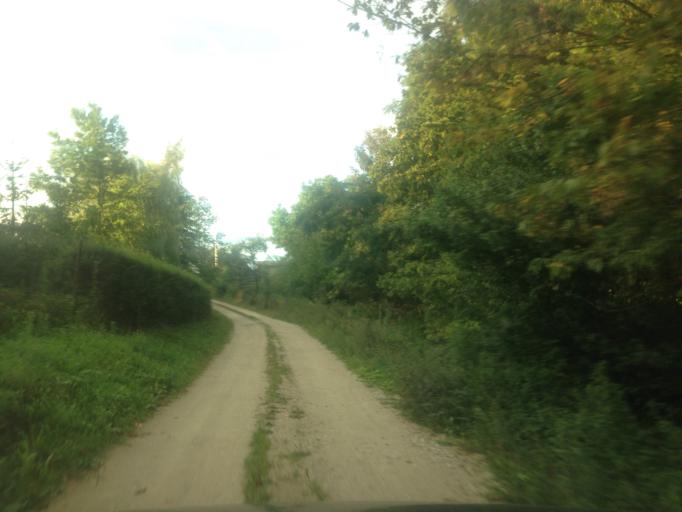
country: PL
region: Kujawsko-Pomorskie
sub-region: Powiat brodnicki
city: Gorzno
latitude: 53.1993
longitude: 19.6626
